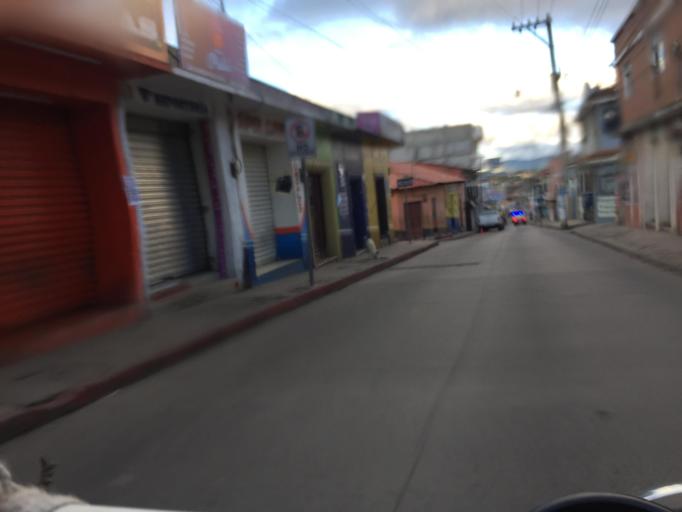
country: GT
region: Totonicapan
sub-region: Municipio de Totonicapan
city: Totonicapan
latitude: 14.9116
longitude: -91.3637
